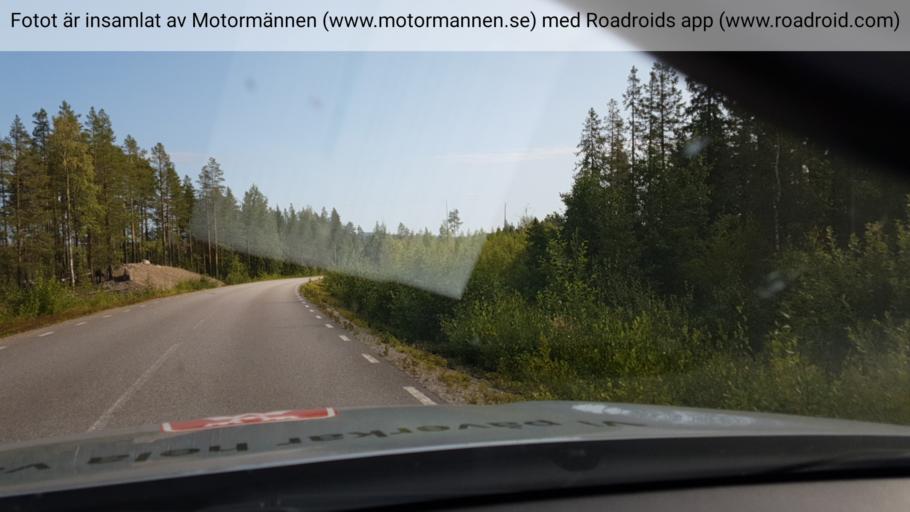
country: SE
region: Norrbotten
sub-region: Alvsbyns Kommun
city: AElvsbyn
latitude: 65.5453
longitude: 20.6086
